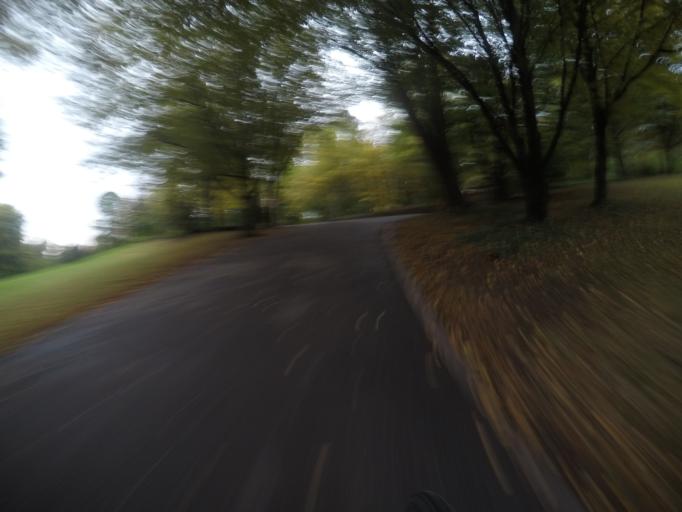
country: DE
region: Baden-Wuerttemberg
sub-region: Regierungsbezirk Stuttgart
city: Stuttgart-Ost
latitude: 48.7931
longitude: 9.2101
